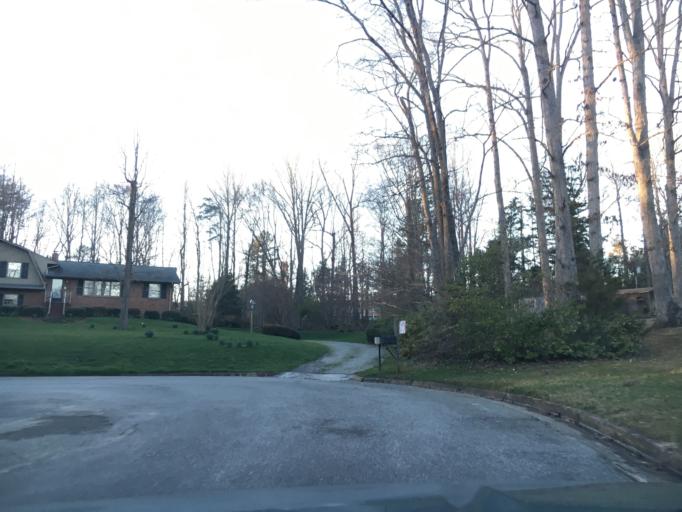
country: US
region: Virginia
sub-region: Halifax County
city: South Boston
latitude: 36.7228
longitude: -78.9162
